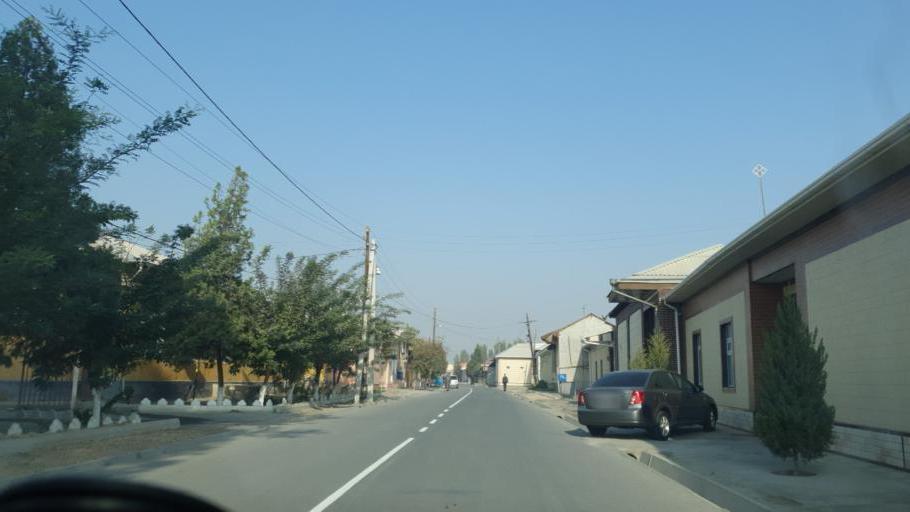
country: UZ
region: Fergana
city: Qo`qon
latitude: 40.5801
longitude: 70.9131
